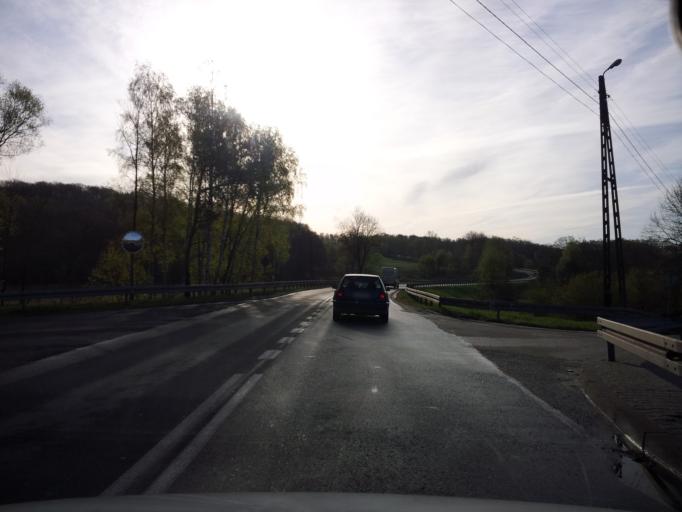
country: PL
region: Lubusz
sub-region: Powiat zielonogorski
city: Nowogrod Bobrzanski
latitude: 51.7983
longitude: 15.2387
